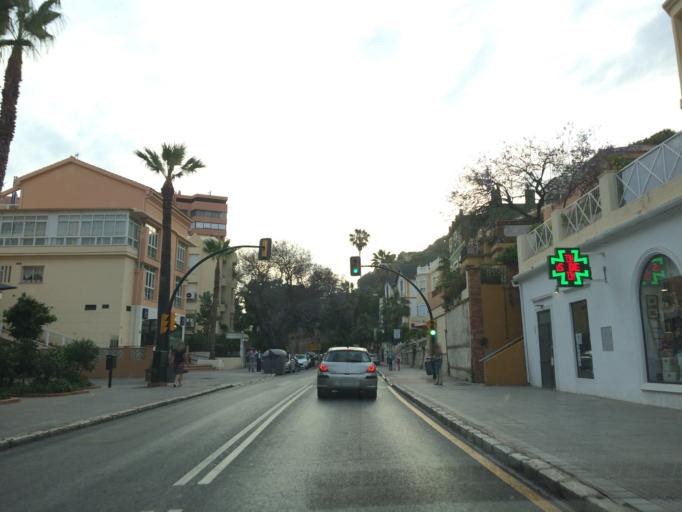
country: ES
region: Andalusia
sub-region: Provincia de Malaga
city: Malaga
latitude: 36.7216
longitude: -4.4031
